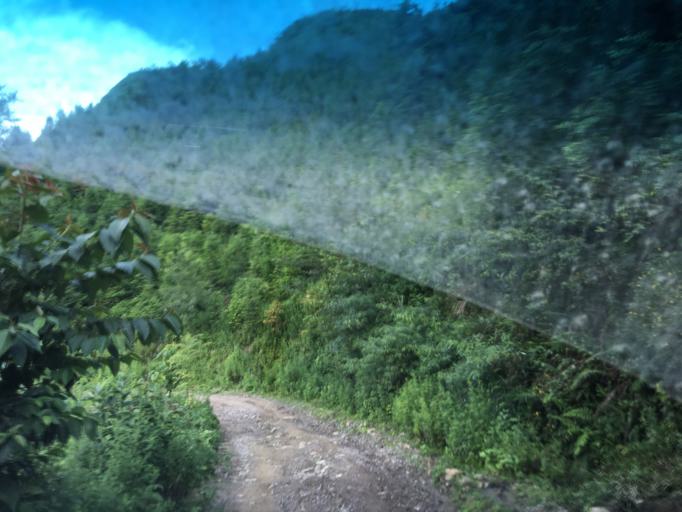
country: CN
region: Guangxi Zhuangzu Zizhiqu
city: Xinzhou
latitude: 24.9898
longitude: 105.6320
